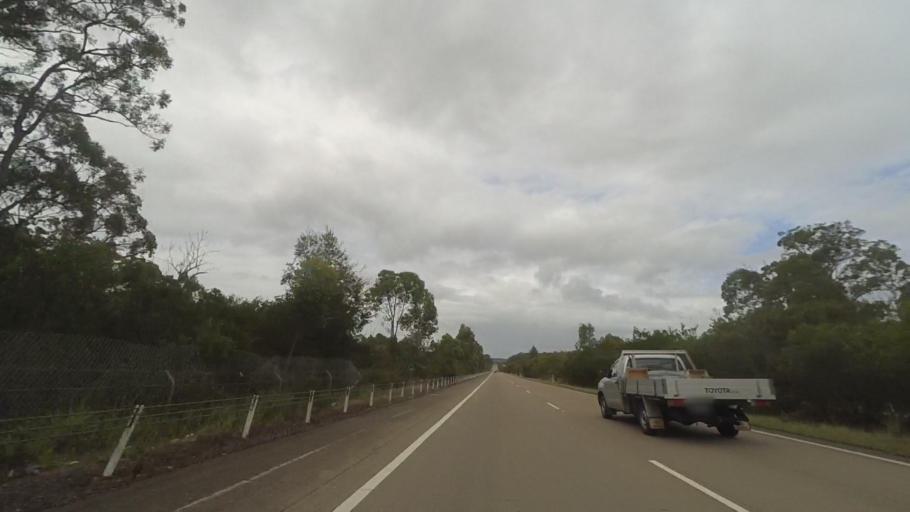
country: AU
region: New South Wales
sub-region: Port Stephens Shire
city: Medowie
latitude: -32.6387
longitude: 151.9322
